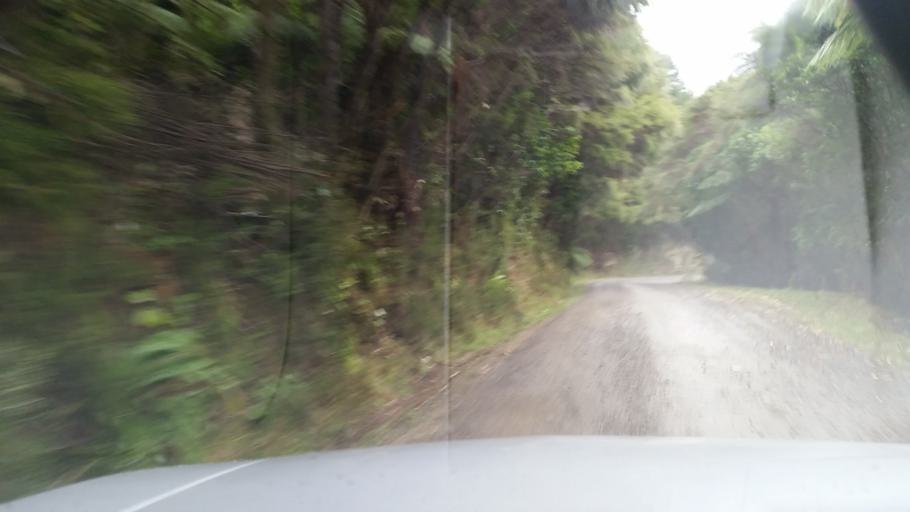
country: NZ
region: Marlborough
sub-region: Marlborough District
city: Picton
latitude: -41.1348
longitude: 174.0492
